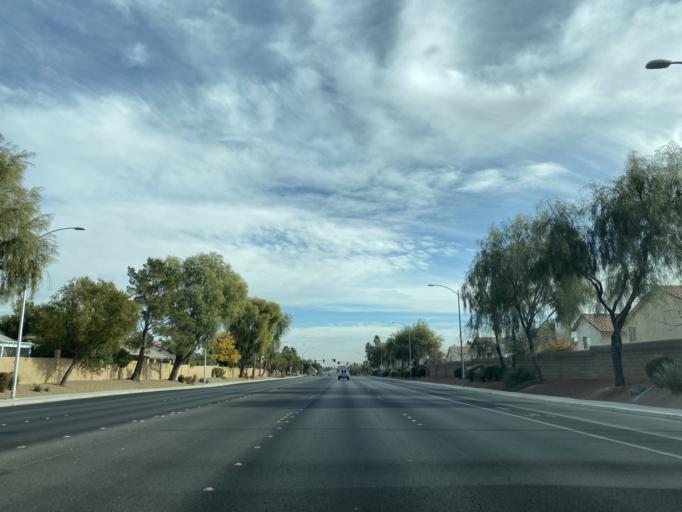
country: US
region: Nevada
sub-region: Clark County
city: Las Vegas
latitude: 36.2464
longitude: -115.2206
